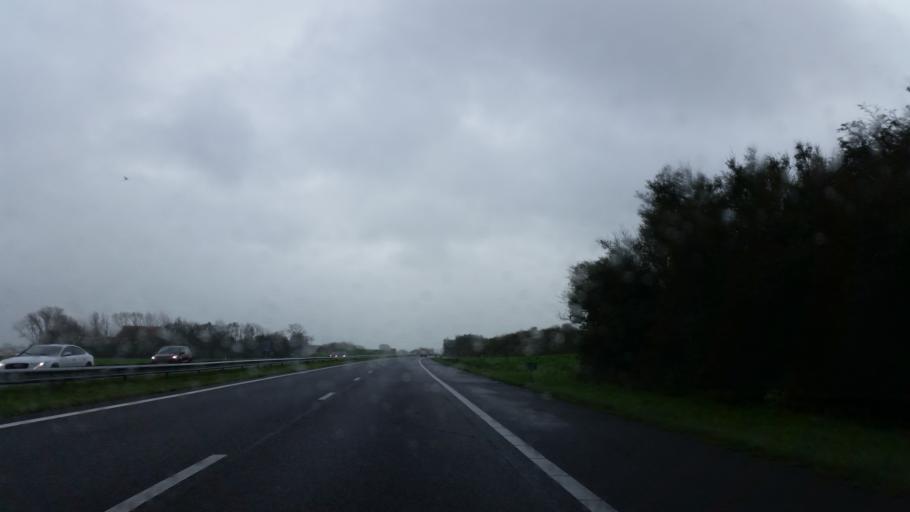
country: NL
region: Friesland
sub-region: Gemeente Boarnsterhim
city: Reduzum
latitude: 53.1098
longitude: 5.8140
